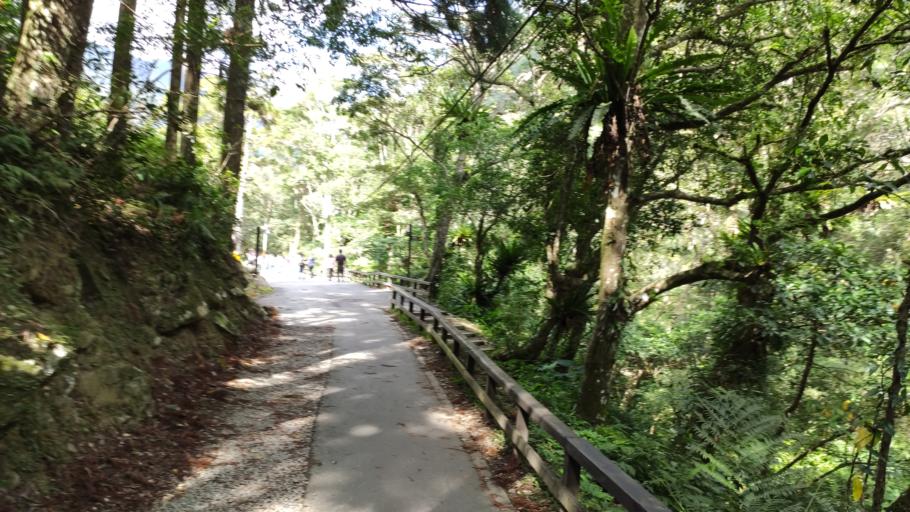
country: TW
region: Taiwan
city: Daxi
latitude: 24.8251
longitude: 121.4491
